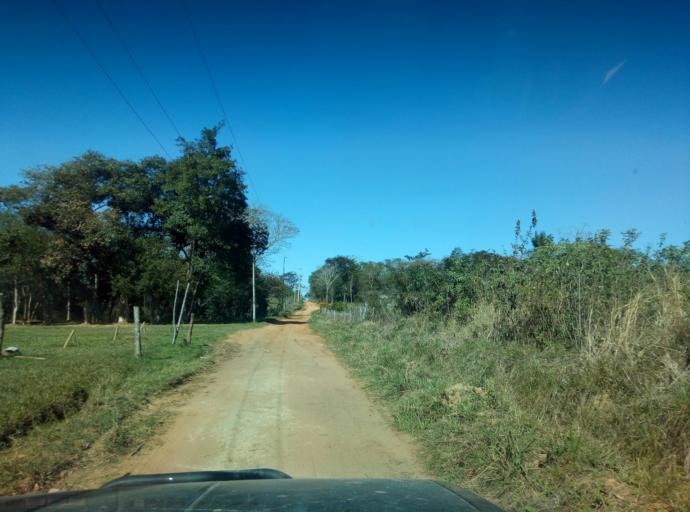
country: PY
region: Caaguazu
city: Doctor Cecilio Baez
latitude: -25.1756
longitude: -56.2020
